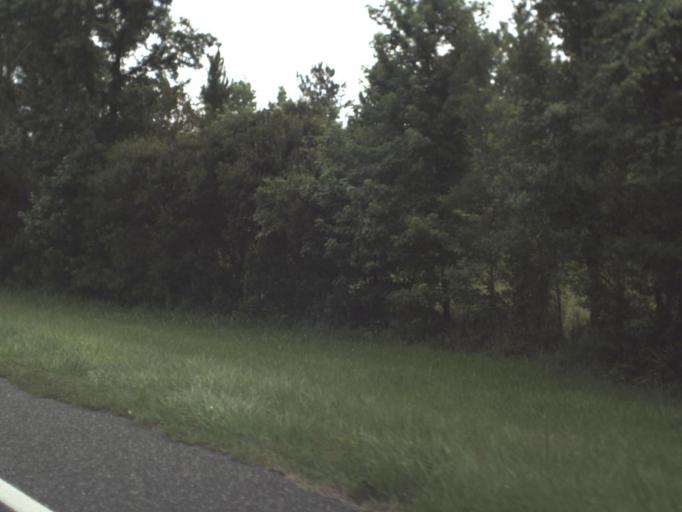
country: US
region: Florida
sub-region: Levy County
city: Bronson
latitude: 29.2963
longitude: -82.7494
